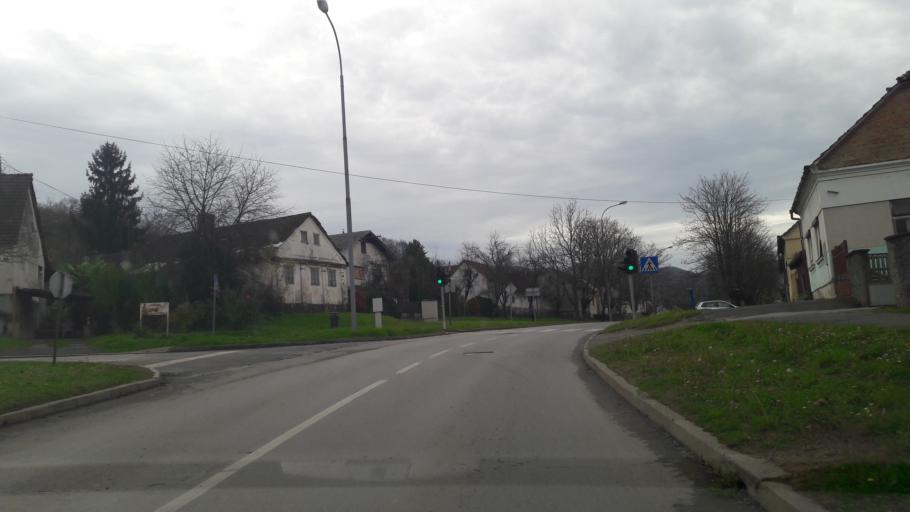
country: HR
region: Virovitick-Podravska
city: Orahovica
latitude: 45.5326
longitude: 17.8868
